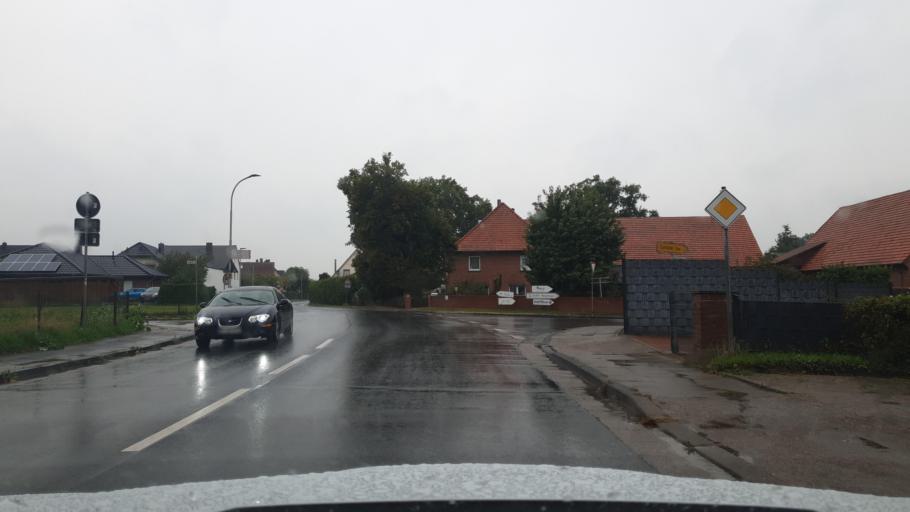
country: DE
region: North Rhine-Westphalia
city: Porta Westfalica
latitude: 52.2159
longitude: 8.8723
